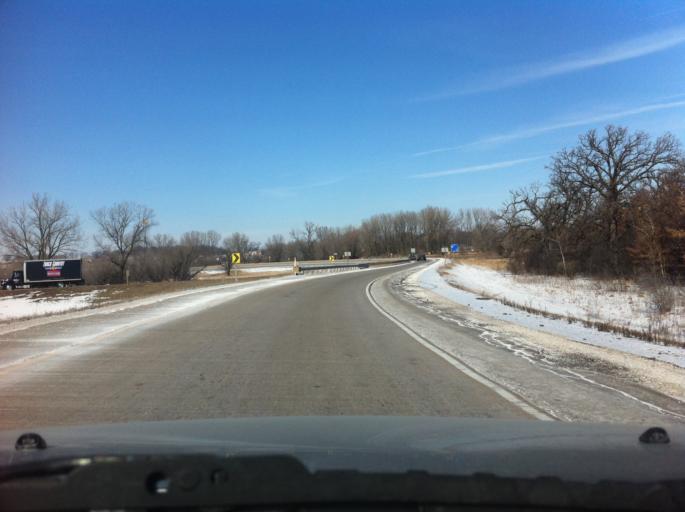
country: US
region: Wisconsin
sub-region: Dane County
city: Windsor
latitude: 43.1719
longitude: -89.3169
